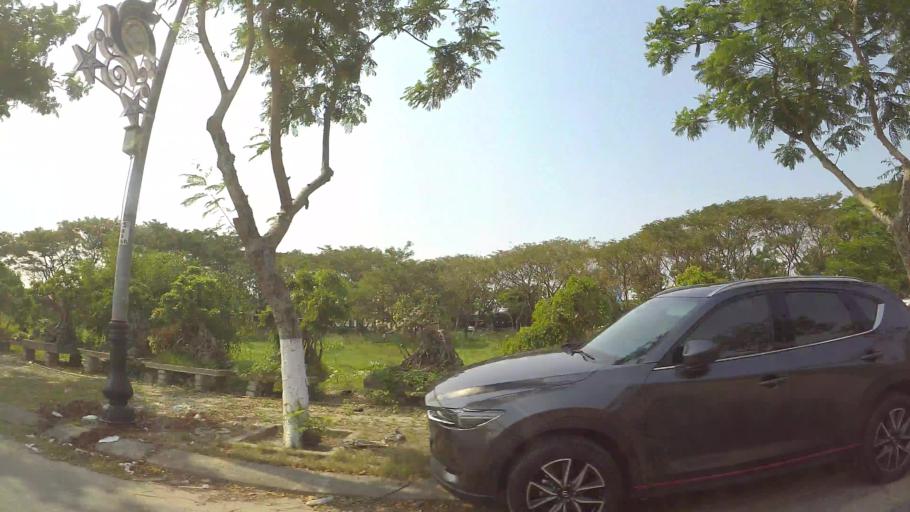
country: VN
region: Da Nang
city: Cam Le
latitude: 16.0110
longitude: 108.2066
